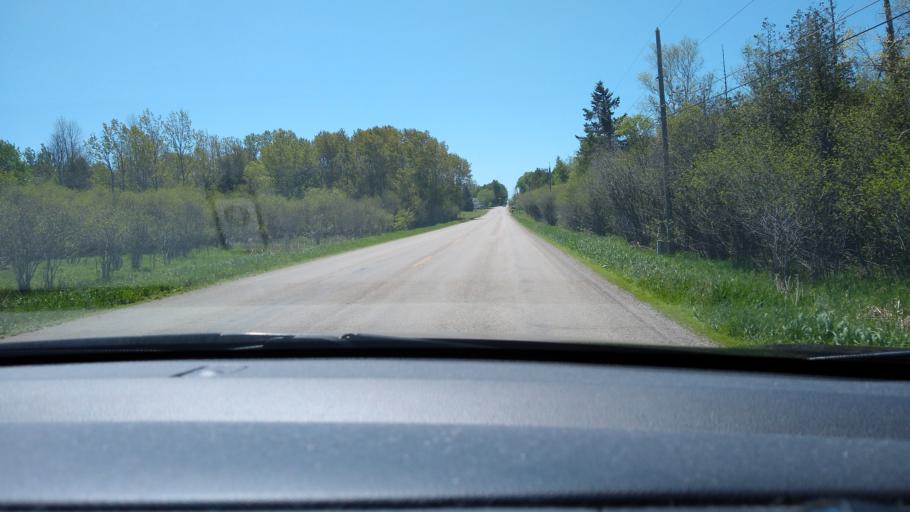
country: US
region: Michigan
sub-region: Delta County
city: Escanaba
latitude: 45.8300
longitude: -87.1833
